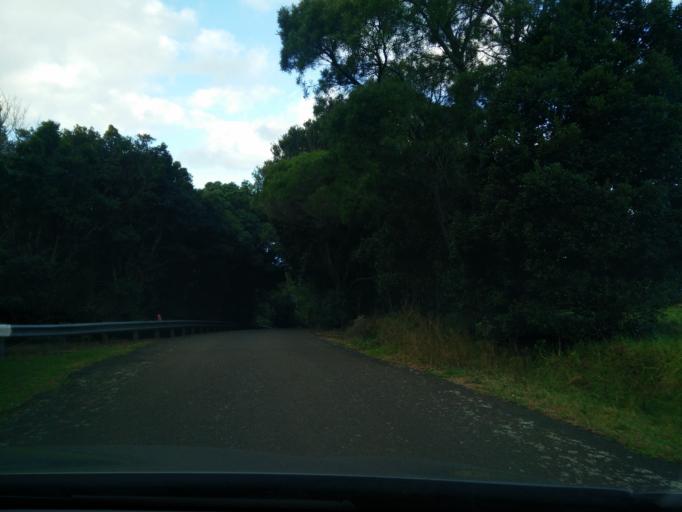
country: AU
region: New South Wales
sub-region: Kiama
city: Jamberoo
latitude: -34.6982
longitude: 150.7942
